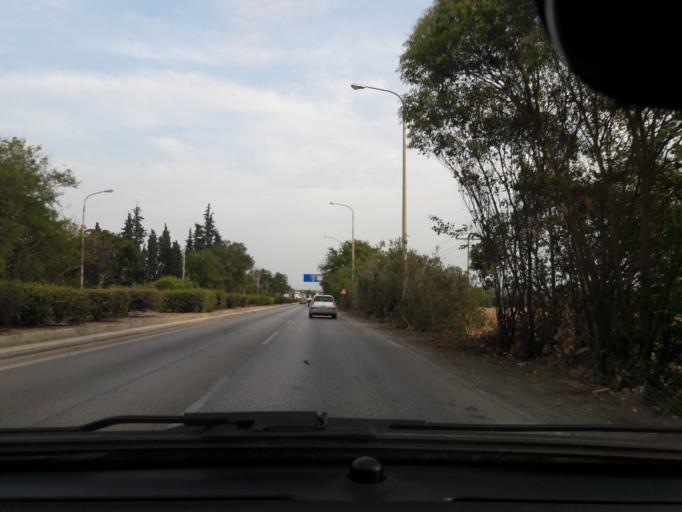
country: GR
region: Central Macedonia
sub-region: Nomos Thessalonikis
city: Thermi
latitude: 40.5358
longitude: 22.9924
